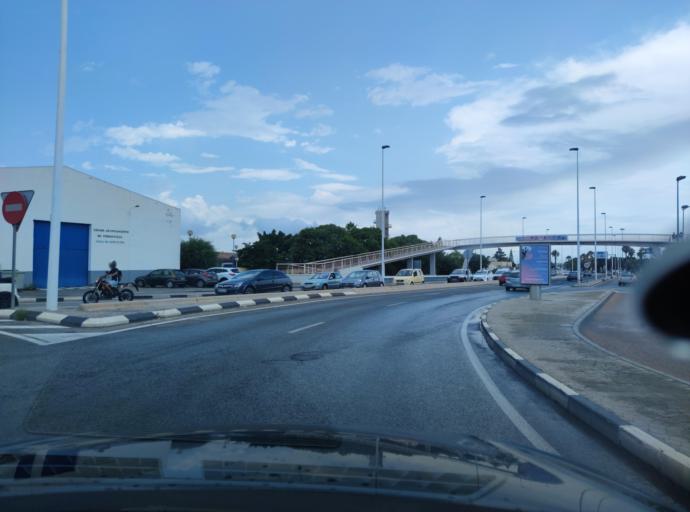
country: ES
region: Valencia
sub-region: Provincia de Alicante
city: Torrevieja
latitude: 37.9894
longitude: -0.6878
